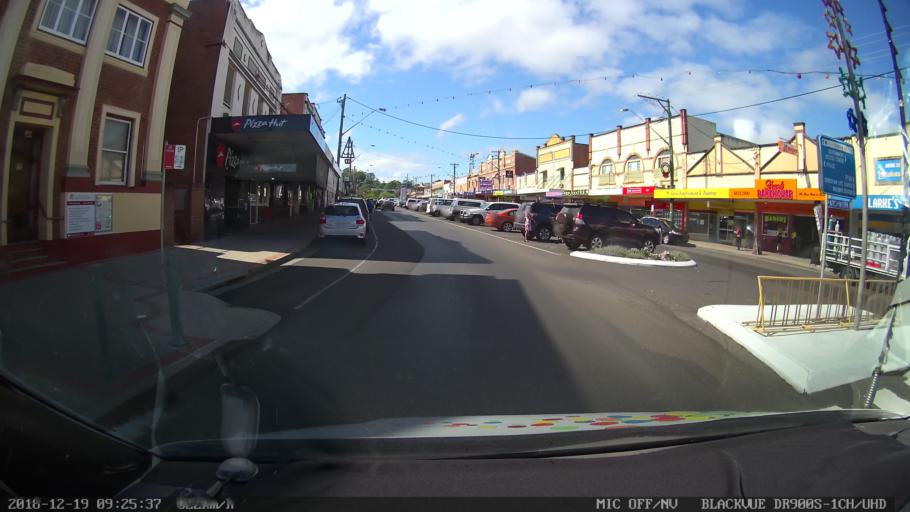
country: AU
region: New South Wales
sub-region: Kyogle
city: Kyogle
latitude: -28.6199
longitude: 153.0038
